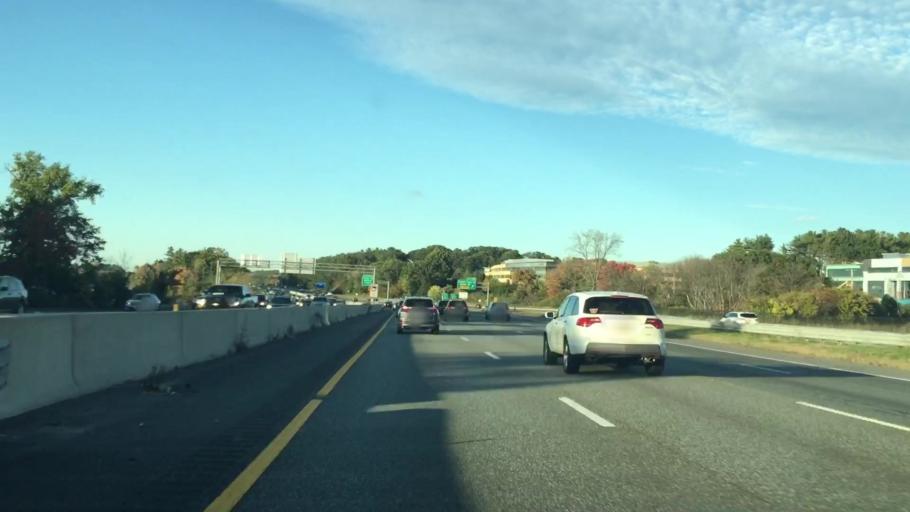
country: US
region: Massachusetts
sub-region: Middlesex County
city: Waltham
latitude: 42.3970
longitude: -71.2614
